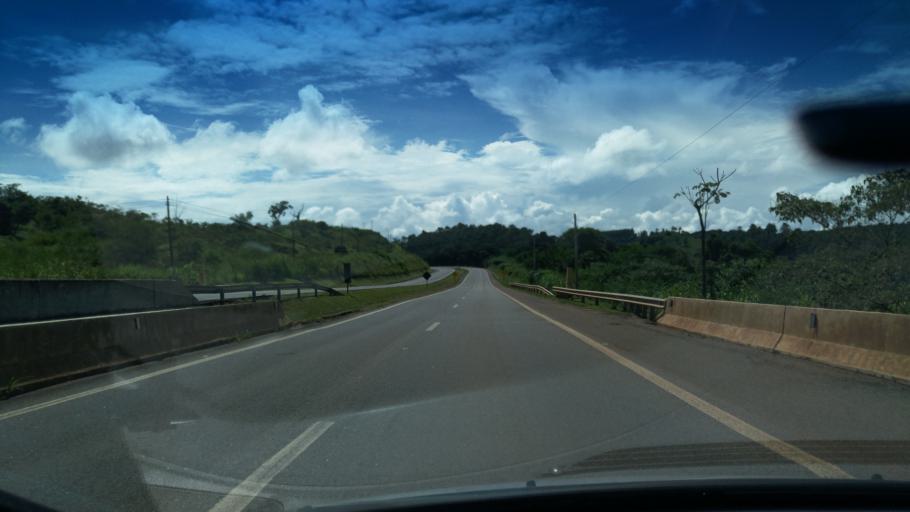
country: BR
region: Sao Paulo
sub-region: Santo Antonio Do Jardim
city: Espirito Santo do Pinhal
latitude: -22.2218
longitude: -46.7909
